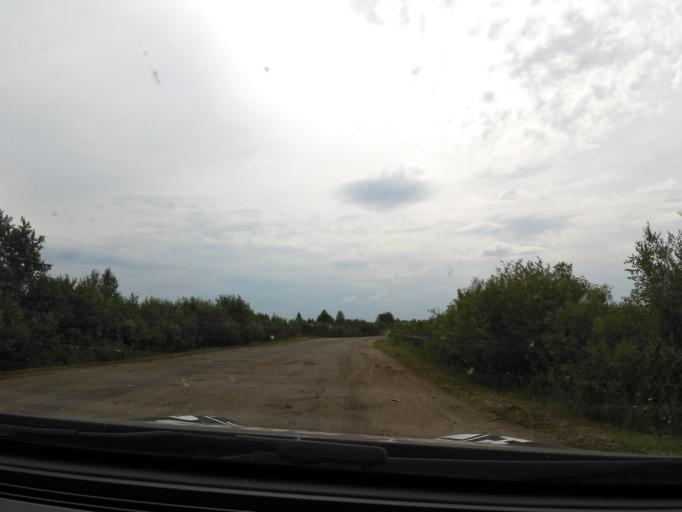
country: RU
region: Kostroma
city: Parfen'yevo
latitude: 58.3414
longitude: 43.4134
